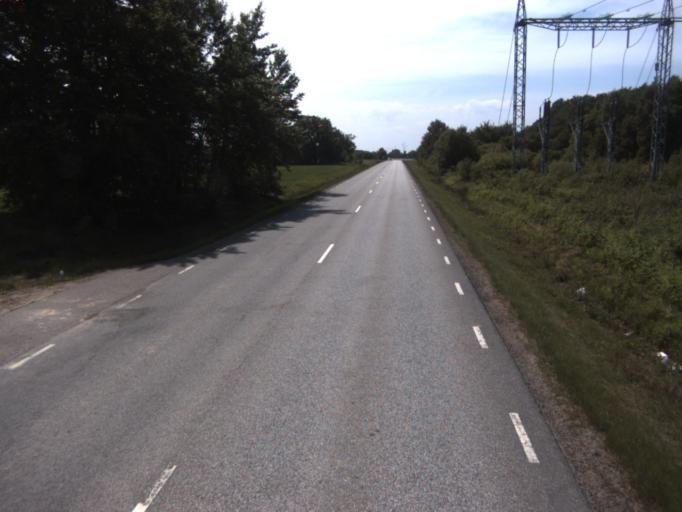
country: SE
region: Skane
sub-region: Helsingborg
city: Helsingborg
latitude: 56.0911
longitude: 12.6714
